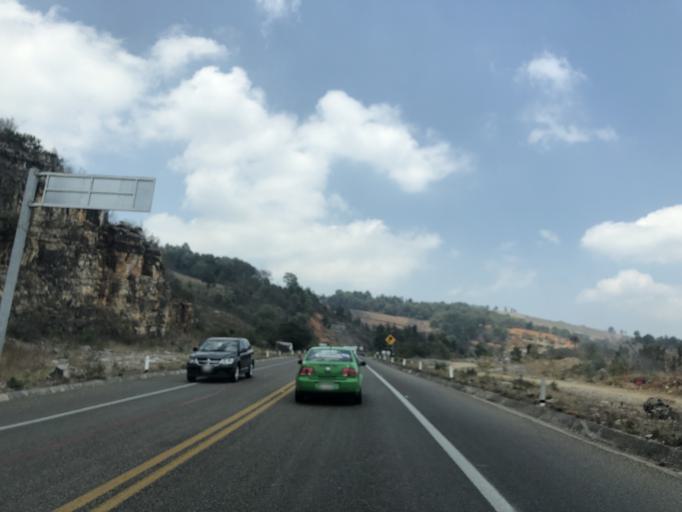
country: MX
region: Chiapas
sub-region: Zinacantan
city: Nachig
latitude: 16.6877
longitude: -92.7320
